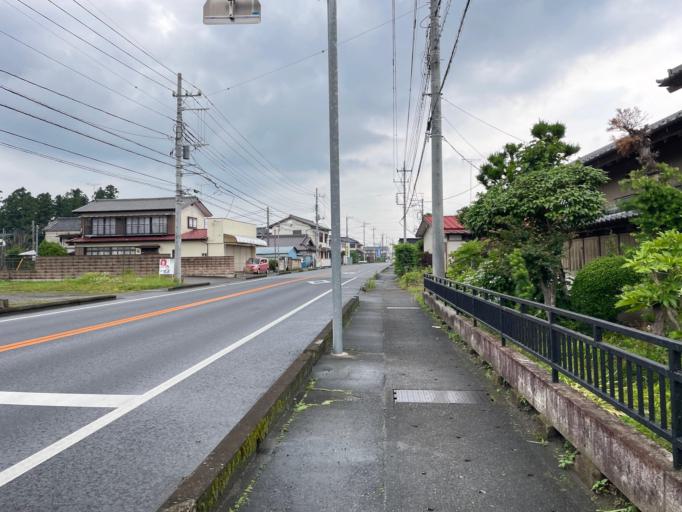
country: JP
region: Tochigi
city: Kanuma
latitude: 36.5215
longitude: 139.7508
